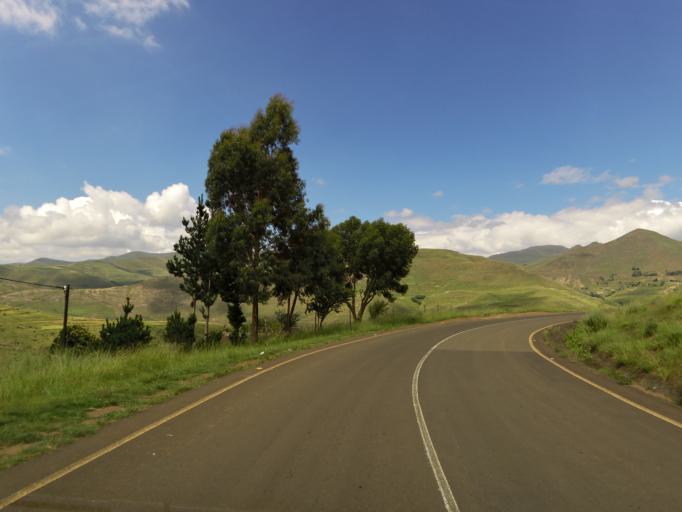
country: LS
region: Thaba-Tseka
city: Thaba-Tseka
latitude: -29.1446
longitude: 28.4912
